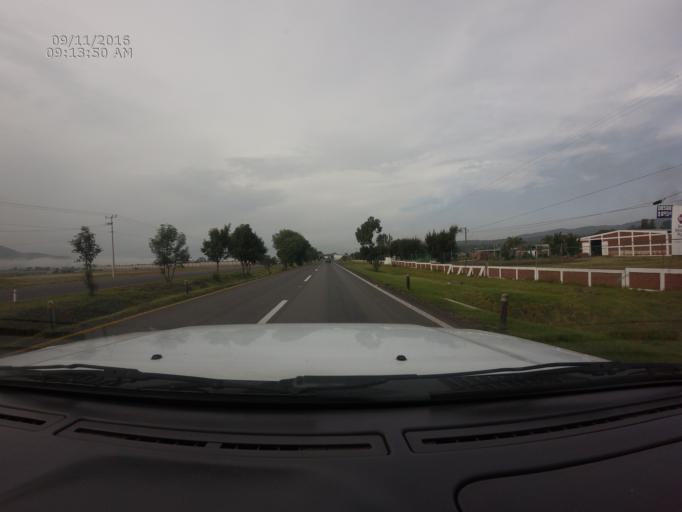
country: MX
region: Michoacan
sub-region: Morelia
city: La Mintzita (Piedra Dura)
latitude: 19.5786
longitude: -101.3119
